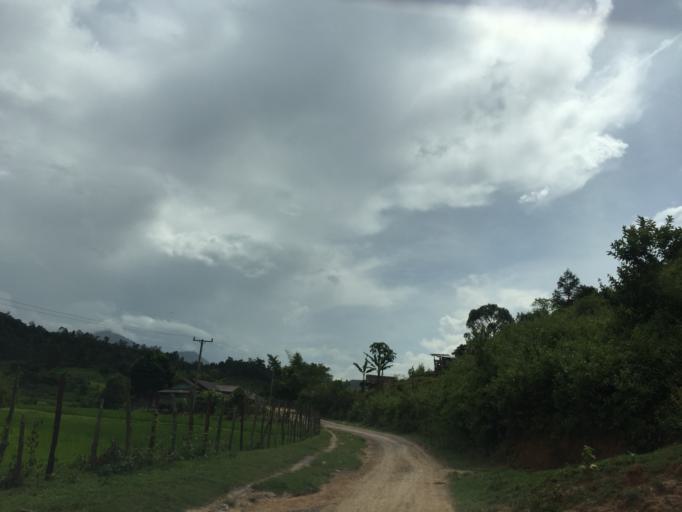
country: LA
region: Xiangkhoang
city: Muang Phonsavan
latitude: 19.3404
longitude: 103.5360
